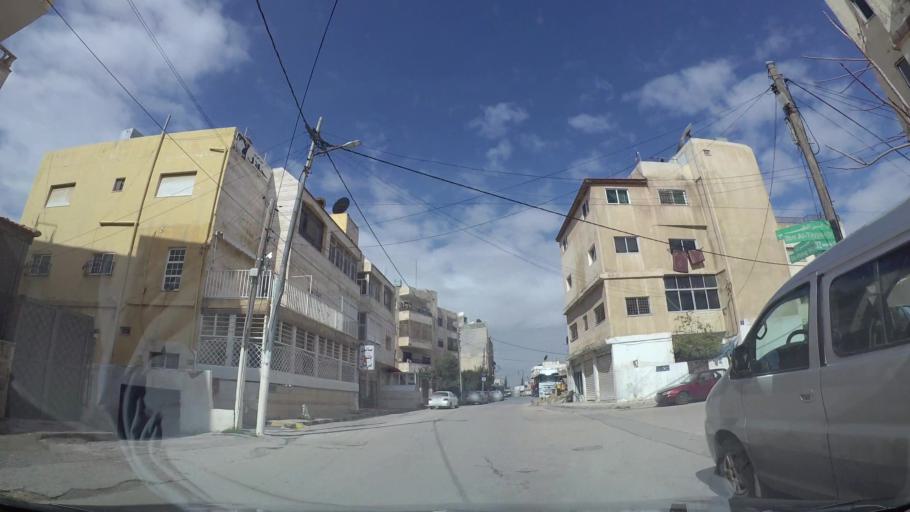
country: JO
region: Amman
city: Wadi as Sir
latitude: 31.9529
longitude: 35.8350
